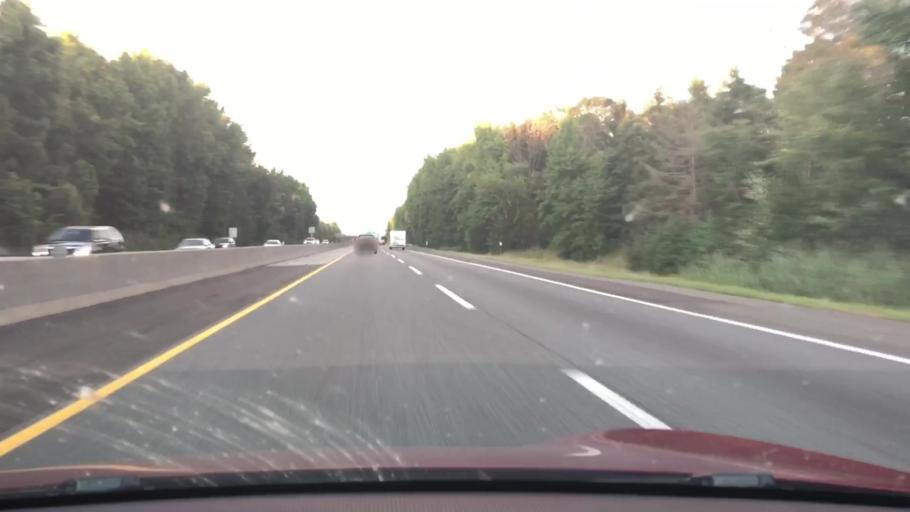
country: US
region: New Jersey
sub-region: Gloucester County
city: Swedesboro
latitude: 39.7475
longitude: -75.2859
